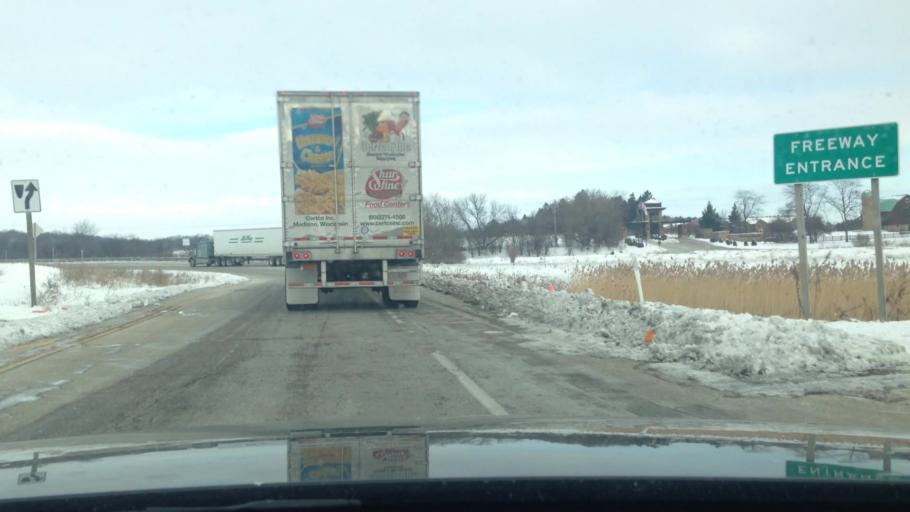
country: US
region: Wisconsin
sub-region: Walworth County
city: Lake Geneva
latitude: 42.5947
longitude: -88.4068
